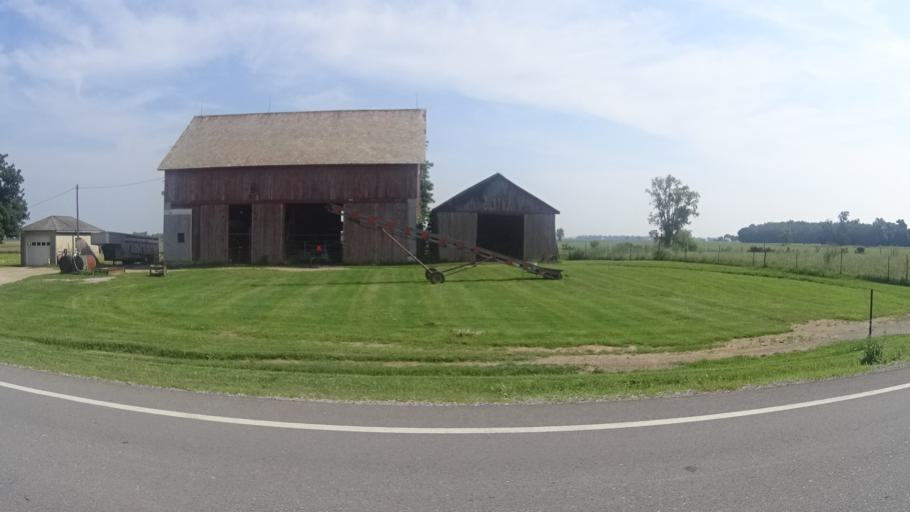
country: US
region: Ohio
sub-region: Huron County
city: Monroeville
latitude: 41.2883
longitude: -82.7427
